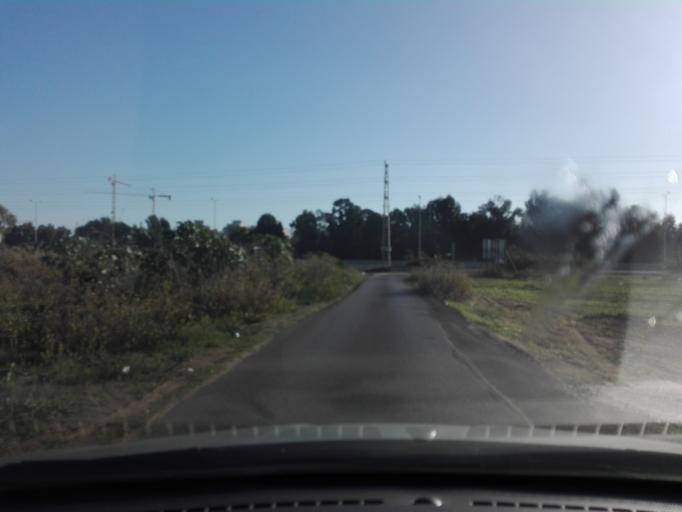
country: IL
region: Central District
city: Netanya
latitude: 32.3084
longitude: 34.8639
